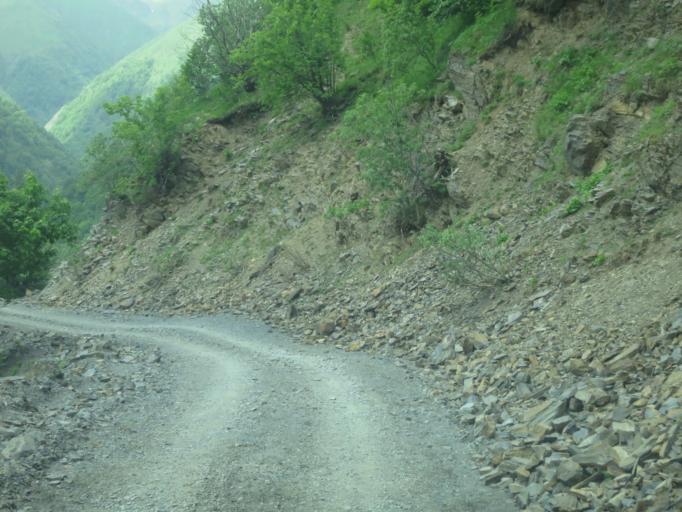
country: GE
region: Kakheti
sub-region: Telavi
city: Telavi
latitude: 42.2521
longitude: 45.4955
